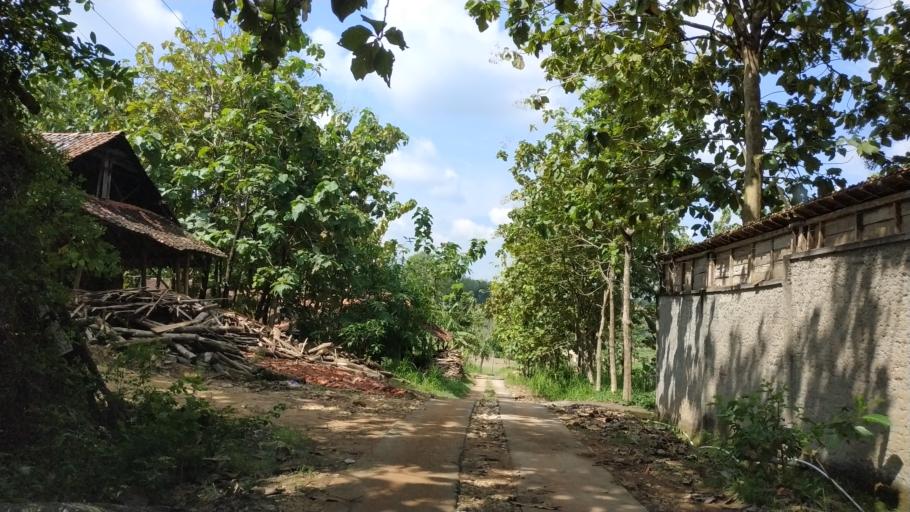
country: ID
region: Central Java
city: Guyangan
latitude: -7.0060
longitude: 111.1033
